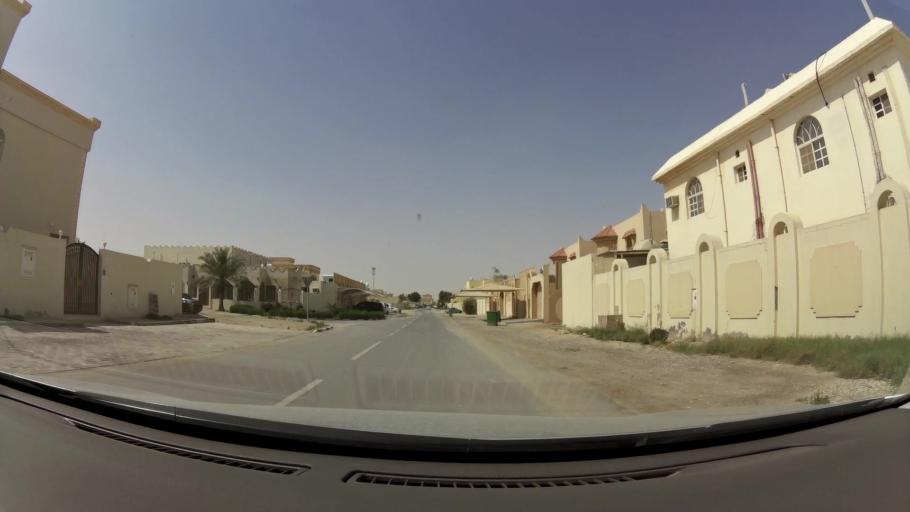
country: QA
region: Baladiyat Umm Salal
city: Umm Salal Muhammad
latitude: 25.3874
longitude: 51.4211
